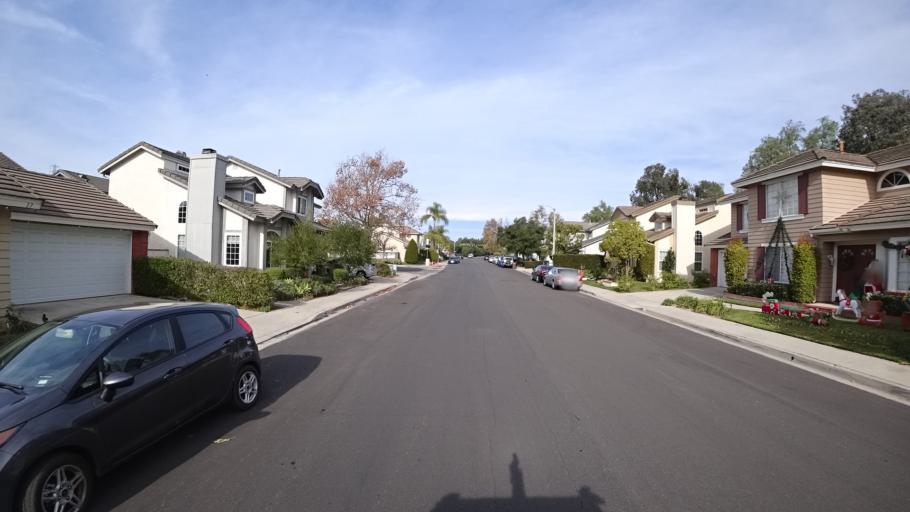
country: US
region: California
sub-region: Orange County
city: Laguna Woods
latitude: 33.5958
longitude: -117.7466
